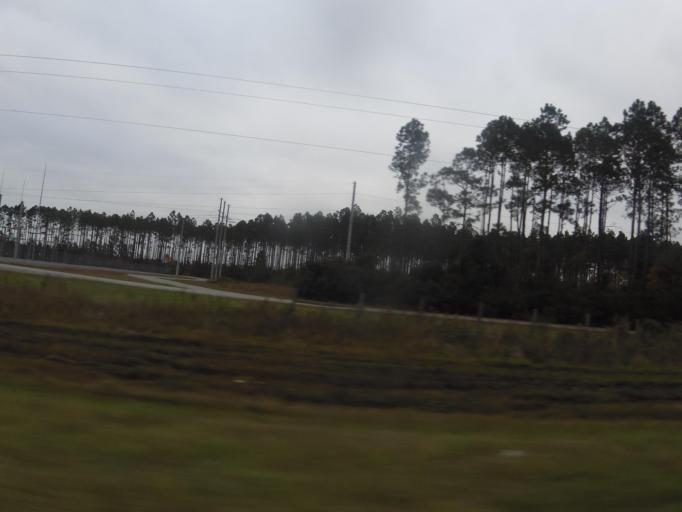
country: US
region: Georgia
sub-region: Charlton County
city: Folkston
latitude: 30.8784
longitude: -82.0320
